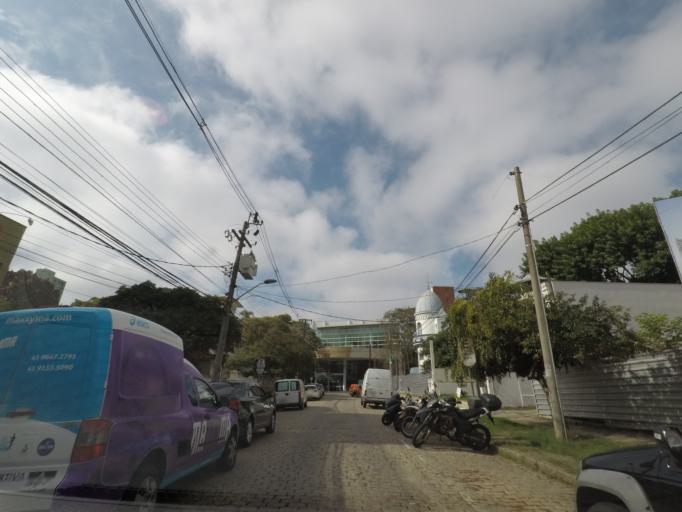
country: BR
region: Parana
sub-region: Curitiba
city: Curitiba
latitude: -25.4381
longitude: -49.2825
